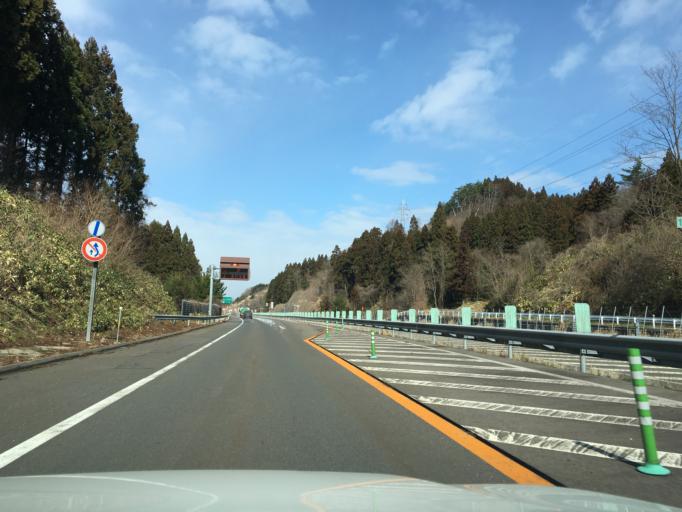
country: JP
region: Akita
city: Akita
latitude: 39.7774
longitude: 140.1177
